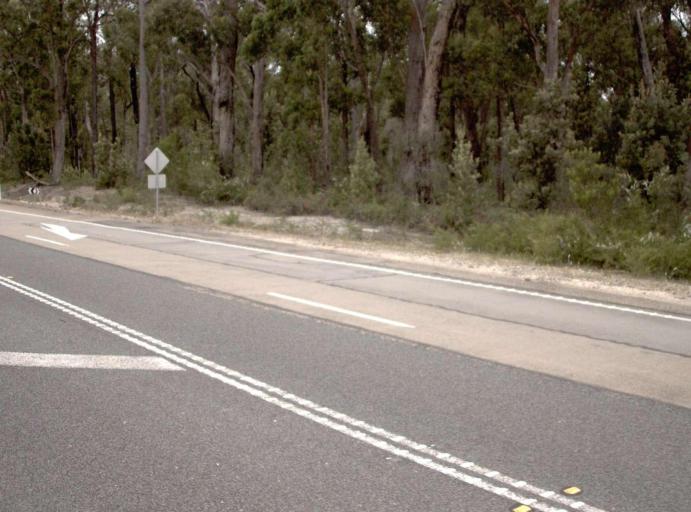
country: AU
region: Victoria
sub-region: East Gippsland
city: Lakes Entrance
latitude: -37.6995
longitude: 147.9938
